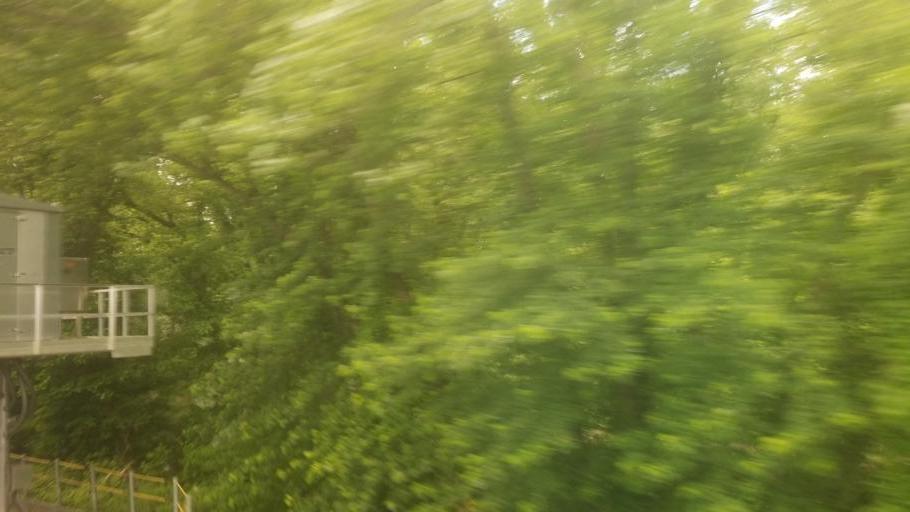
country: US
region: Maryland
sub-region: Frederick County
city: Brunswick
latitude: 39.3102
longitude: -77.6239
